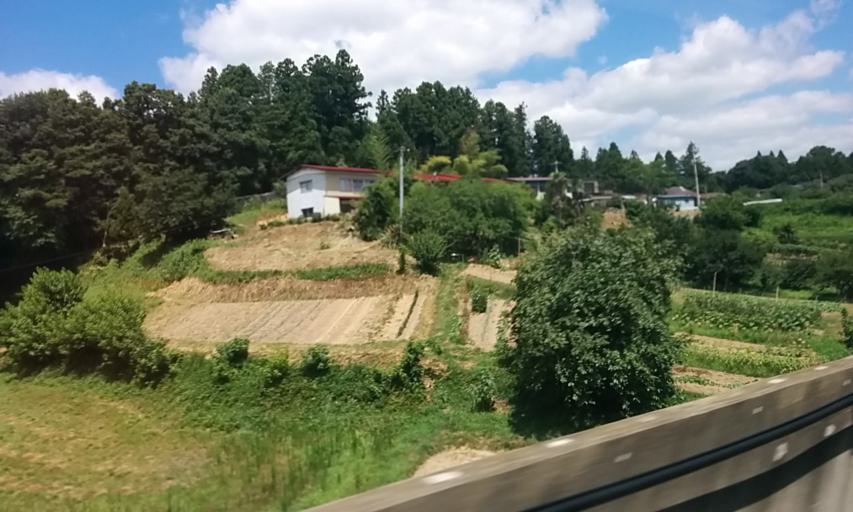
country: JP
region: Fukushima
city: Nihommatsu
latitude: 37.5527
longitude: 140.4518
